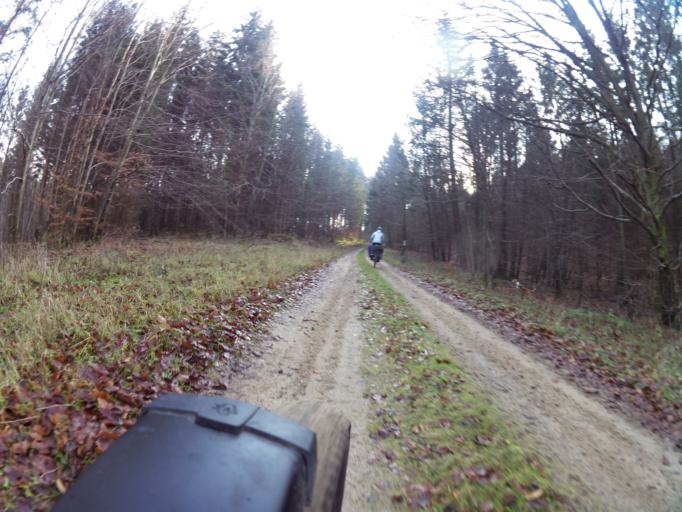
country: PL
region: West Pomeranian Voivodeship
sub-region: Powiat koszalinski
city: Polanow
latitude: 54.1723
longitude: 16.7269
